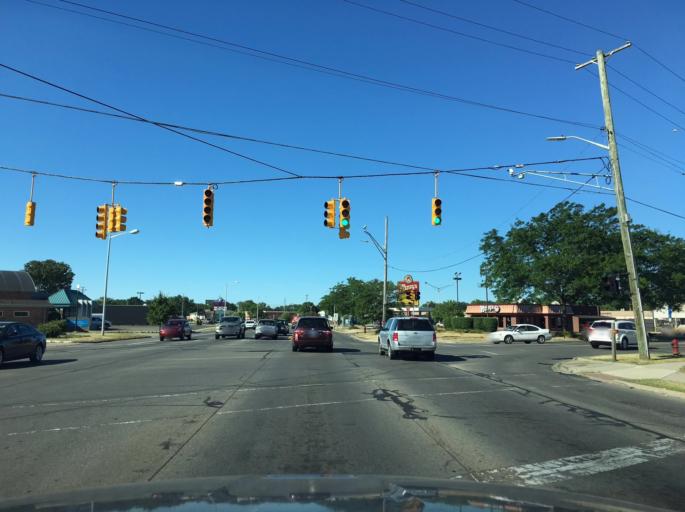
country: US
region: Michigan
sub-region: Macomb County
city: Saint Clair Shores
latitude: 42.5252
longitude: -82.8973
